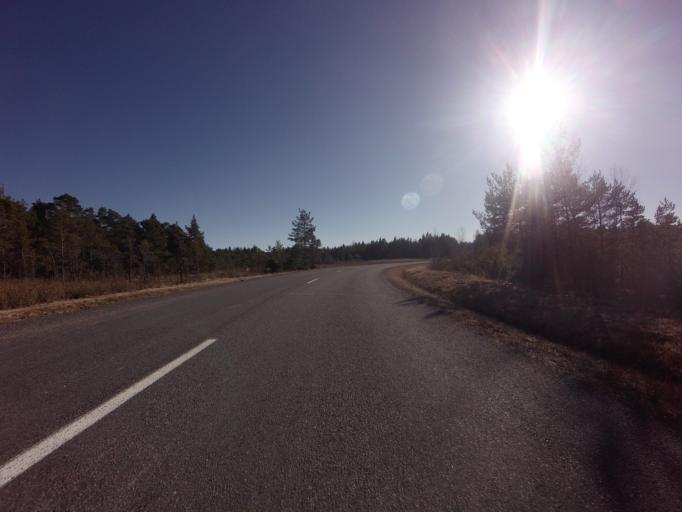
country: EE
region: Saare
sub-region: Kuressaare linn
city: Kuressaare
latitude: 58.5071
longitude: 22.3134
